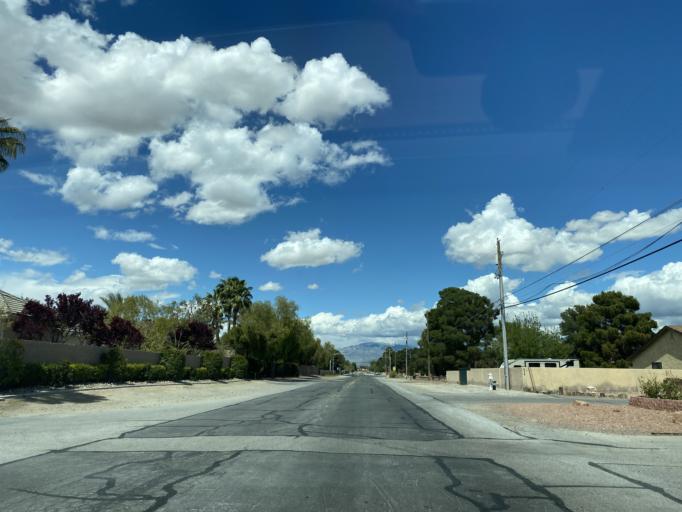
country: US
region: Nevada
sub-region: Clark County
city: Spring Valley
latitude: 36.2457
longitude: -115.2698
